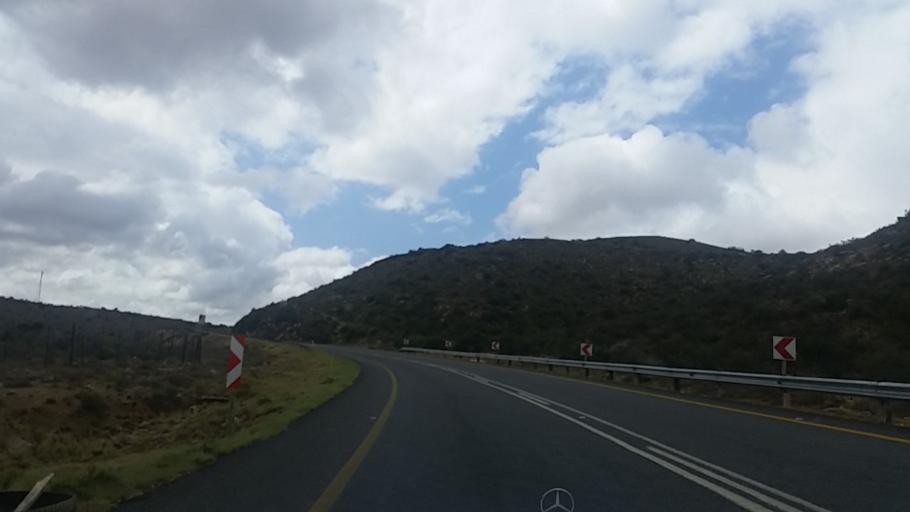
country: ZA
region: Eastern Cape
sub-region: Cacadu District Municipality
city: Graaff-Reinet
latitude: -32.1172
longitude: 24.6083
